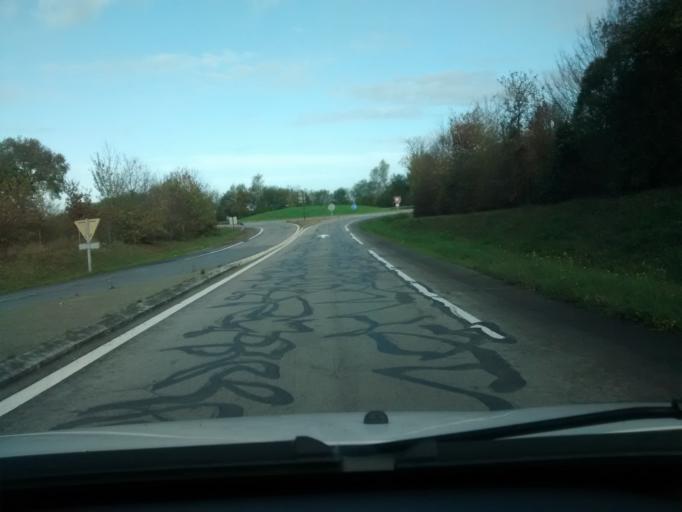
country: FR
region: Brittany
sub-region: Departement d'Ille-et-Vilaine
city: Acigne
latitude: 48.1172
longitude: -1.5677
